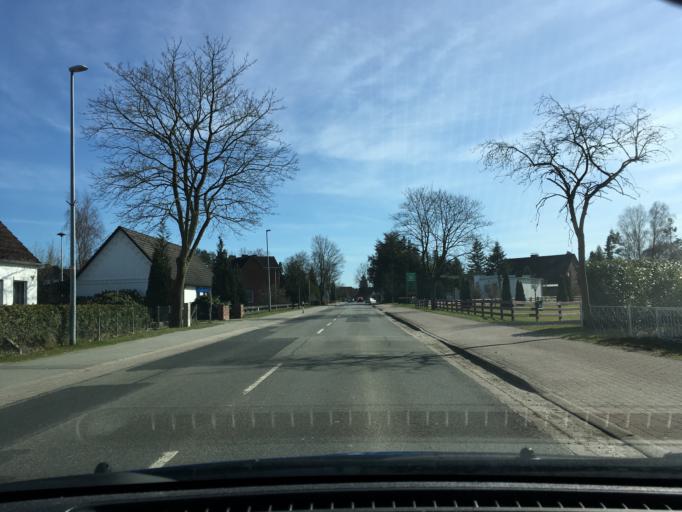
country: DE
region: Lower Saxony
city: Tespe
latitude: 53.3964
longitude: 10.4109
